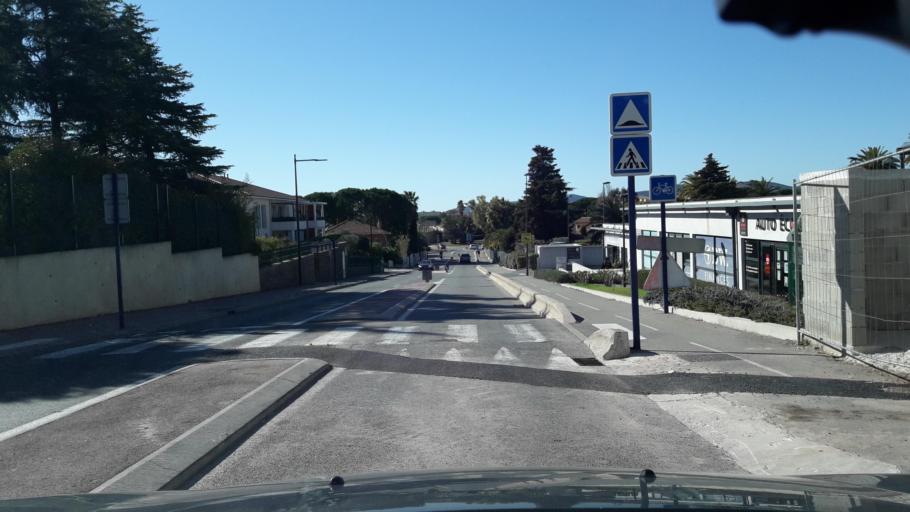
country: FR
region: Provence-Alpes-Cote d'Azur
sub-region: Departement du Var
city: Frejus
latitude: 43.4398
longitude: 6.7565
